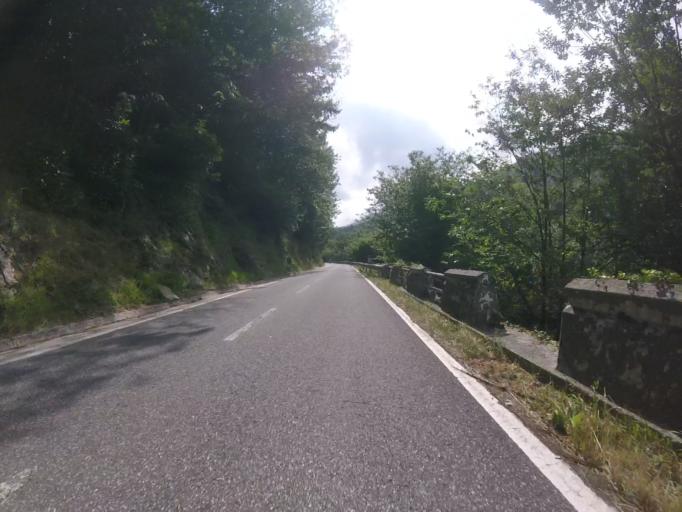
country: ES
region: Navarre
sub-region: Provincia de Navarra
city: Eratsun
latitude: 43.0847
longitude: -1.8081
